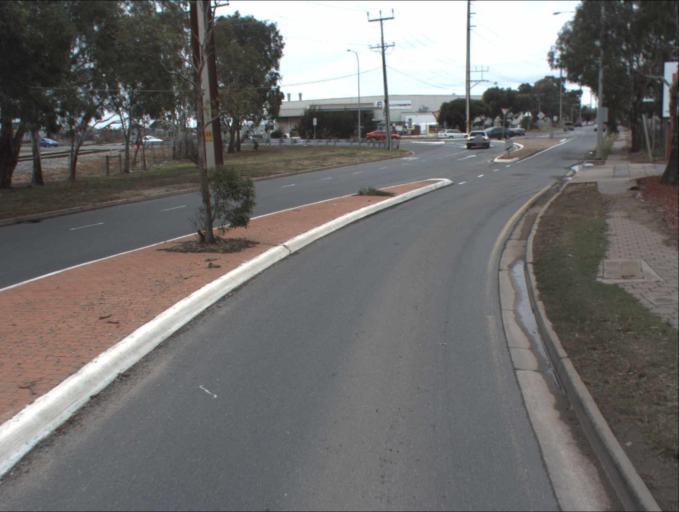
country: AU
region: South Australia
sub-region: Port Adelaide Enfield
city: Blair Athol
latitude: -34.8414
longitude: 138.5823
